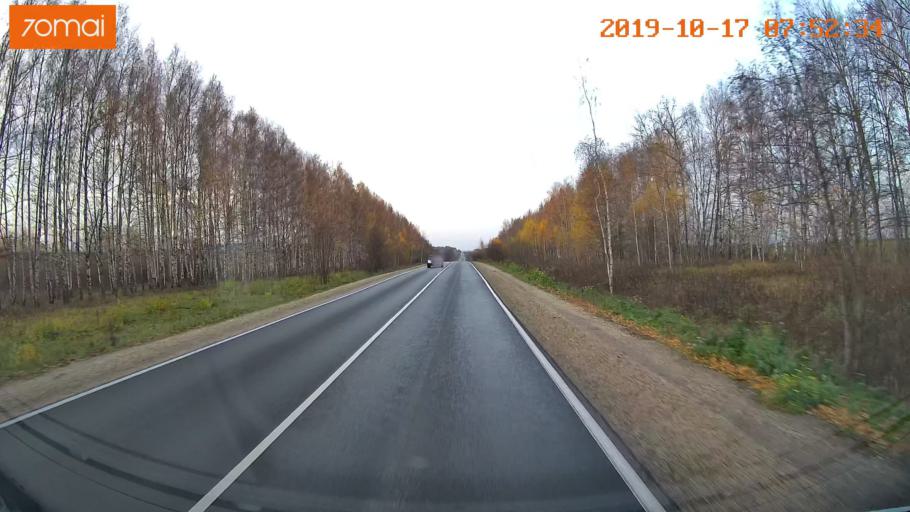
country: RU
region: Vladimir
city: Yur'yev-Pol'skiy
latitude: 56.4713
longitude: 39.6382
